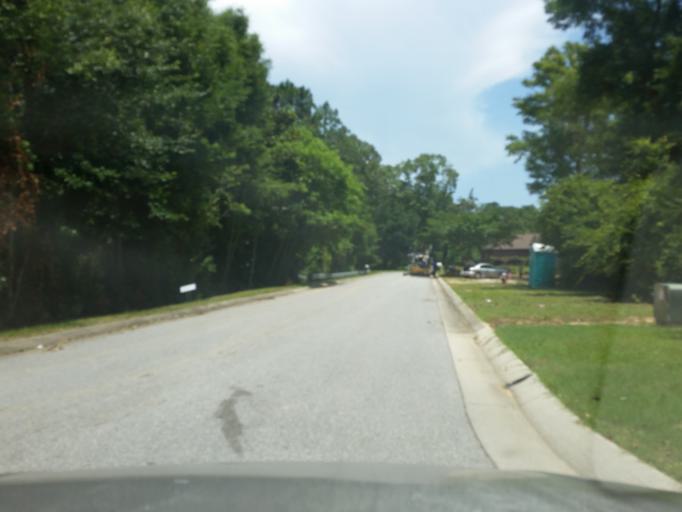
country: US
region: Florida
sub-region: Escambia County
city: Ferry Pass
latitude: 30.5328
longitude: -87.1987
